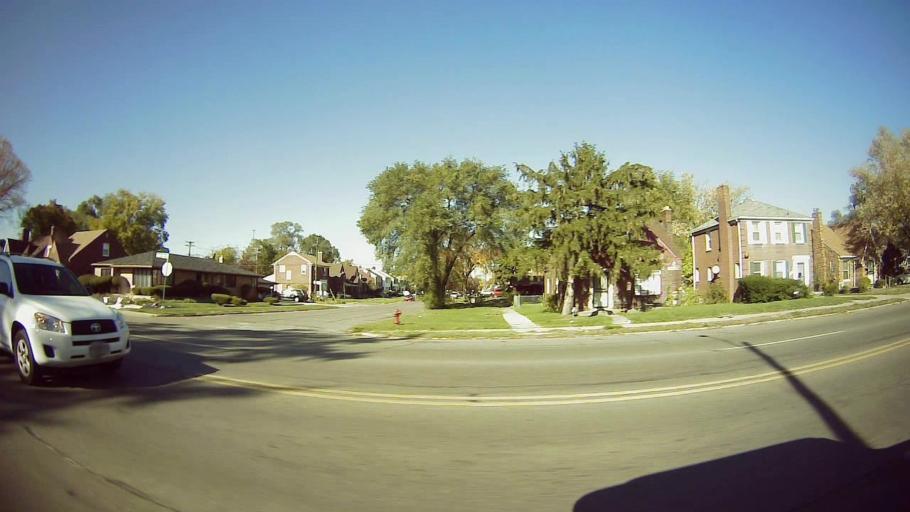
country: US
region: Michigan
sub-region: Oakland County
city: Oak Park
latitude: 42.4314
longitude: -83.1586
